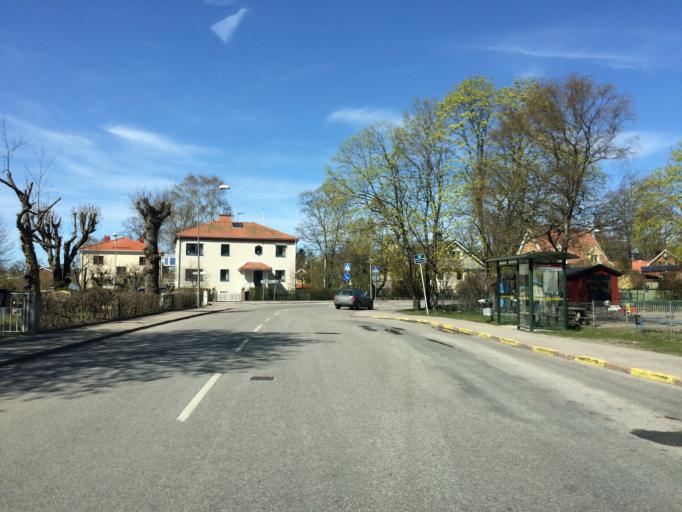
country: SE
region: Stockholm
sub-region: Huddinge Kommun
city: Segeltorp
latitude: 59.2750
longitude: 17.9614
